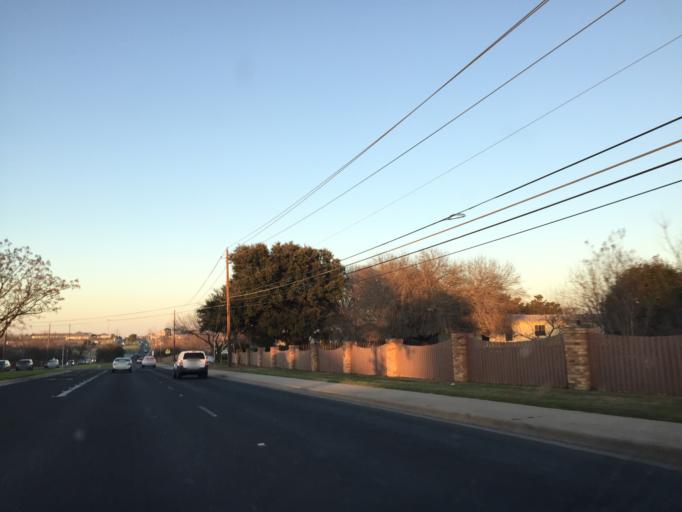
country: US
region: Texas
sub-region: Travis County
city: Pflugerville
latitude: 30.3938
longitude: -97.6448
